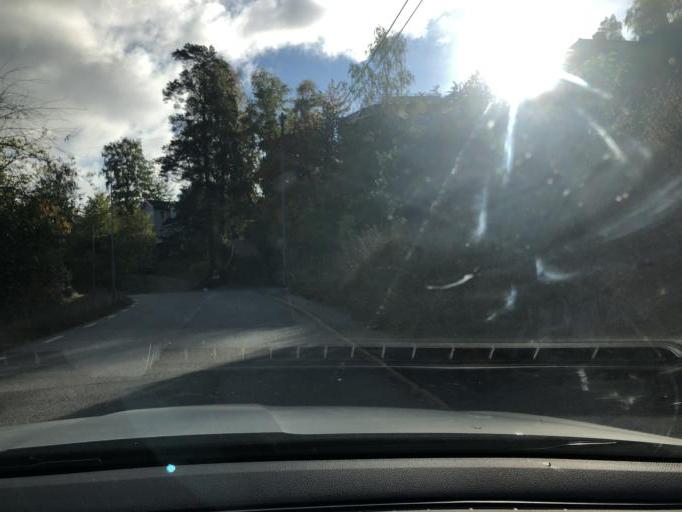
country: SE
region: Stockholm
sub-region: Nacka Kommun
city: Nacka
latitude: 59.2990
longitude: 18.1534
